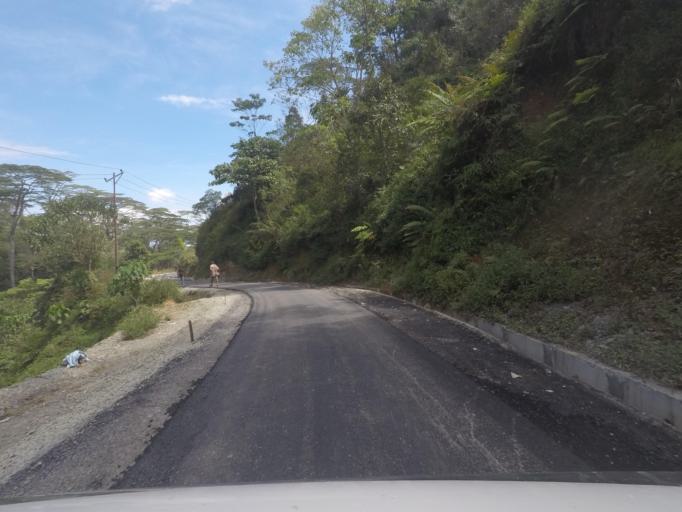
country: TL
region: Ermera
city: Gleno
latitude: -8.7533
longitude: 125.3350
